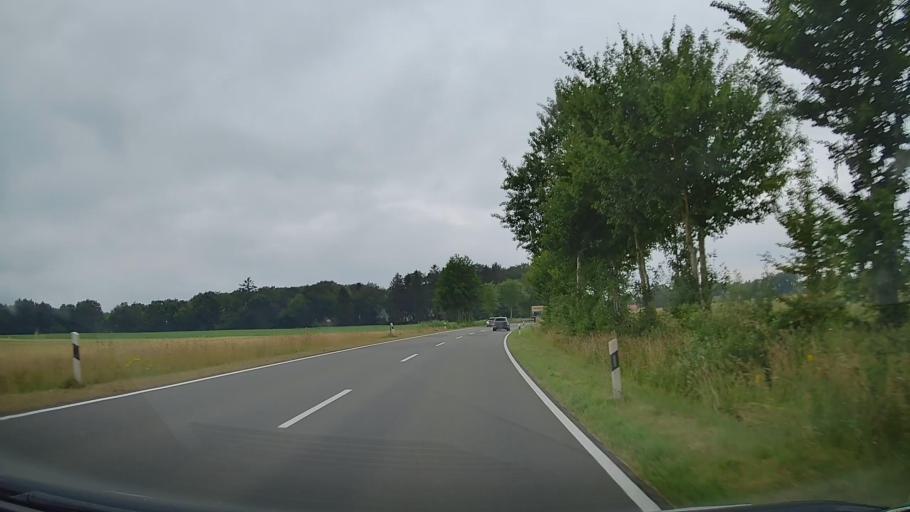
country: DE
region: Lower Saxony
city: Dinklage
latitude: 52.6770
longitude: 8.0775
